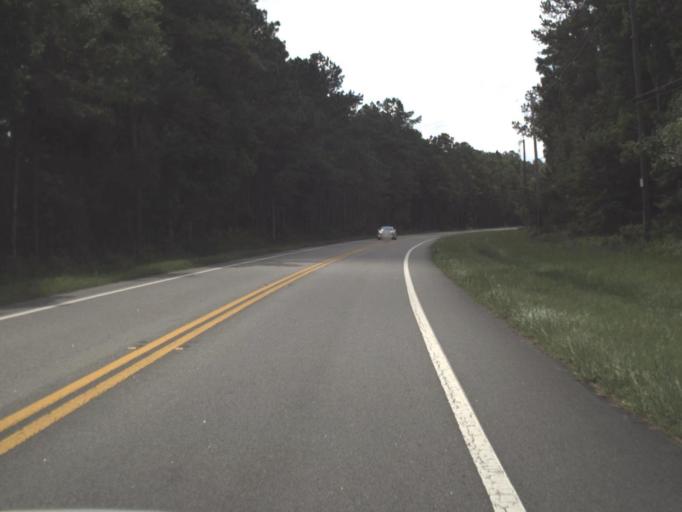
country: US
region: Florida
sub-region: Clay County
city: Green Cove Springs
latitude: 30.0356
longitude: -81.6508
